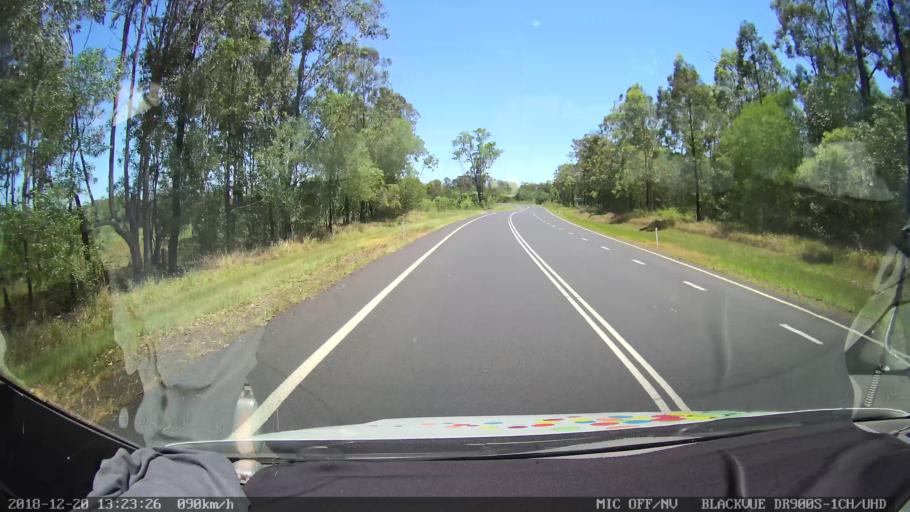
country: AU
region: New South Wales
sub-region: Richmond Valley
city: Casino
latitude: -29.1046
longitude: 152.9999
